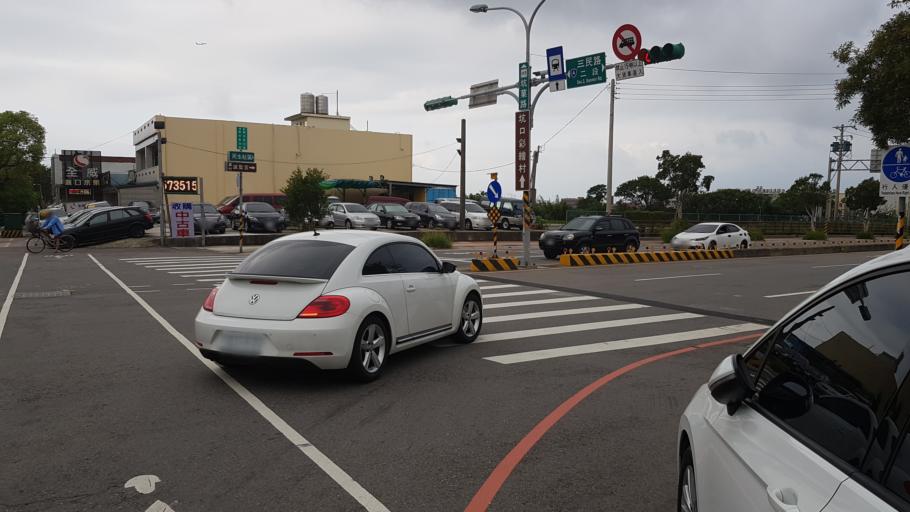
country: TW
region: Taiwan
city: Taoyuan City
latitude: 25.0790
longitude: 121.2592
